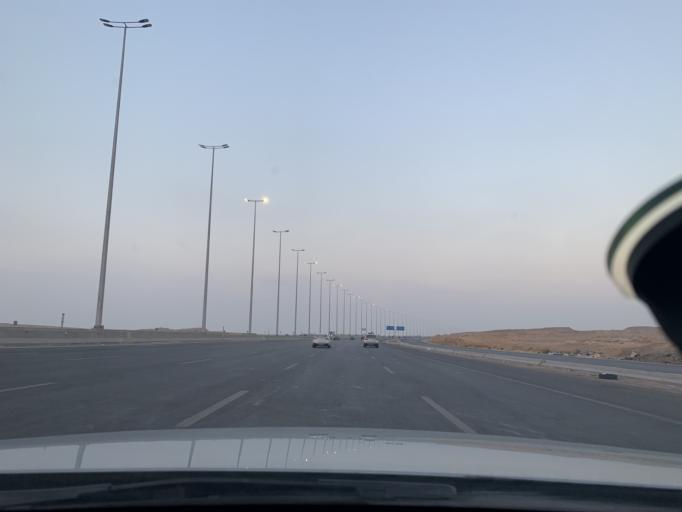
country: EG
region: Muhafazat al Qalyubiyah
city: Al Khankah
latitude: 30.0946
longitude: 31.4839
